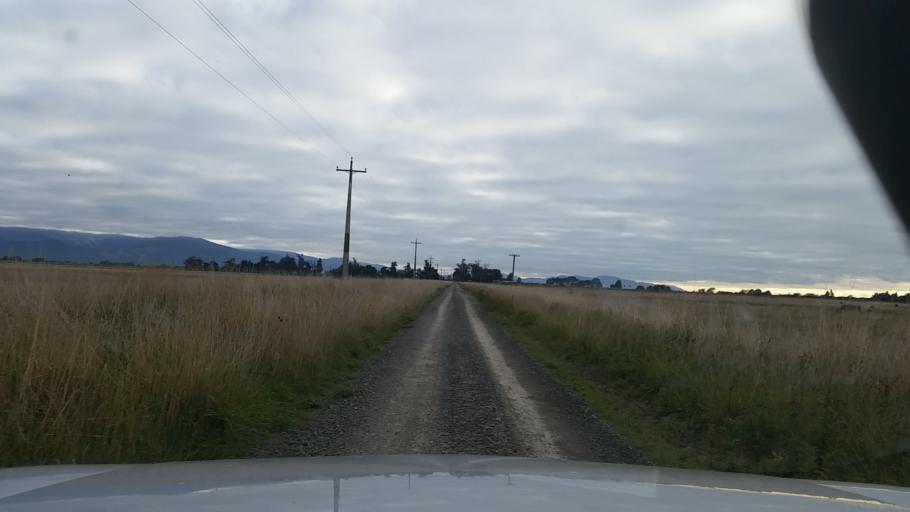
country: NZ
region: Marlborough
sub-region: Marlborough District
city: Blenheim
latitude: -41.5072
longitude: 174.0301
